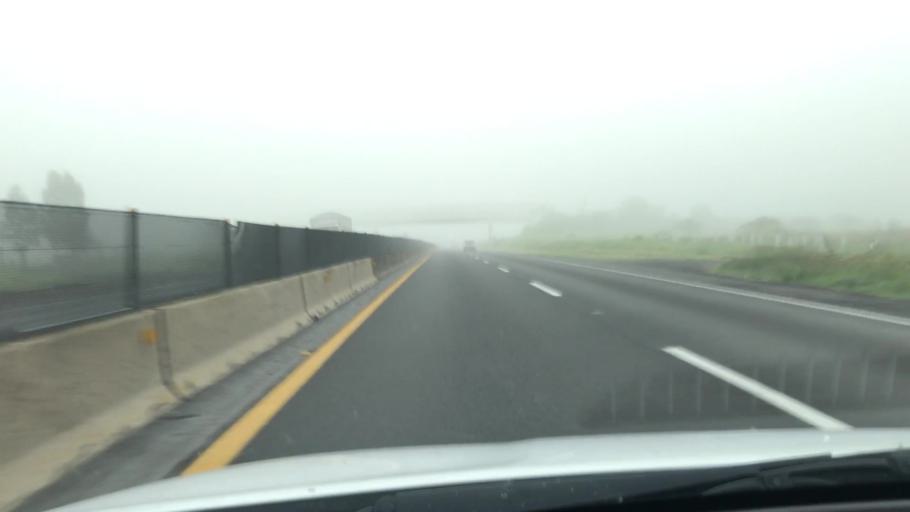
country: MX
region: Jalisco
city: Valle de Guadalupe
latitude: 20.9753
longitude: -102.6166
